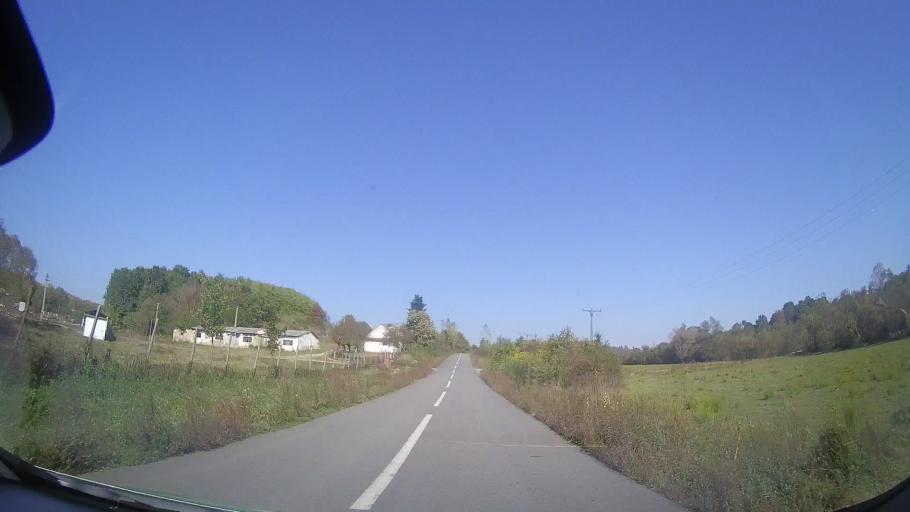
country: RO
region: Timis
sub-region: Comuna Bara
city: Bara
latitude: 45.8765
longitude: 21.8850
